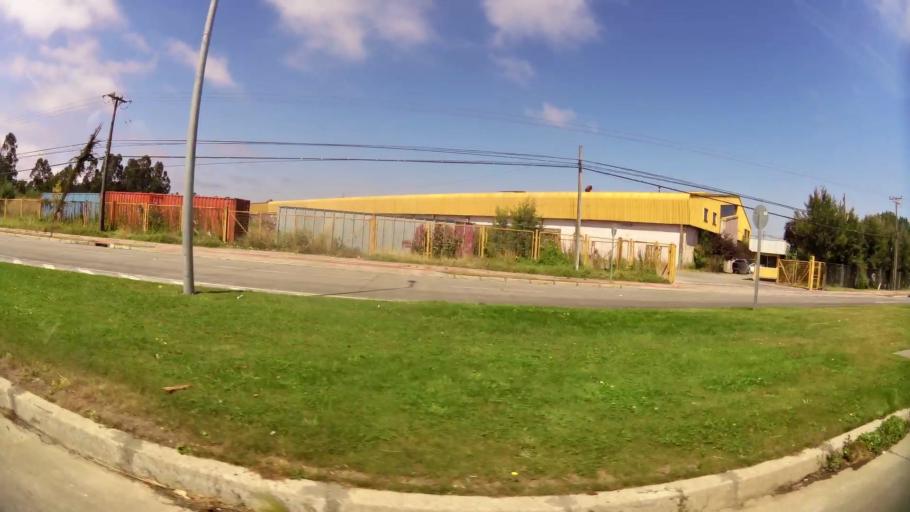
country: CL
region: Biobio
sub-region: Provincia de Concepcion
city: Concepcion
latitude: -36.7868
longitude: -73.0602
